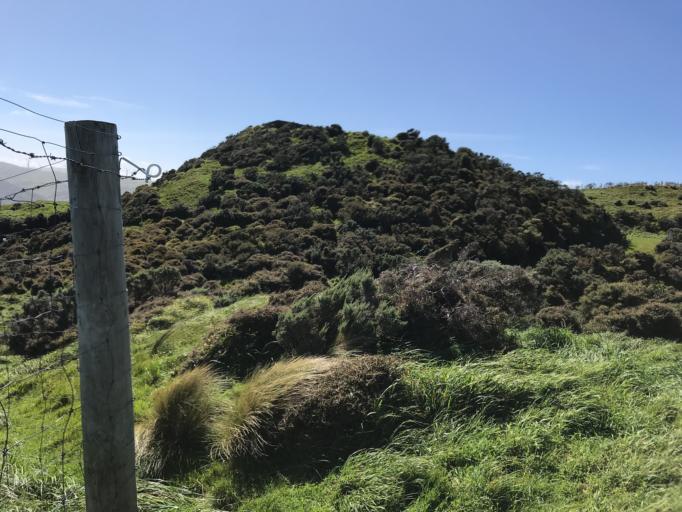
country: NZ
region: Wellington
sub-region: Wellington City
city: Kelburn
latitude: -41.2224
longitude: 174.6960
